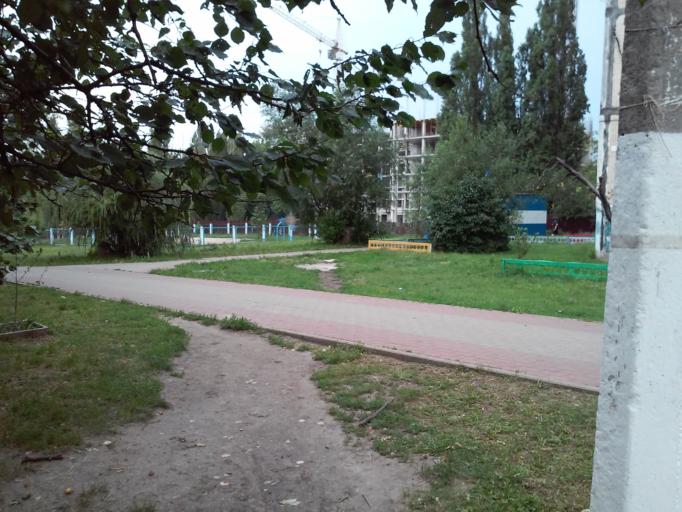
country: RU
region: Belgorod
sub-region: Belgorodskiy Rayon
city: Belgorod
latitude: 50.5714
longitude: 36.5808
